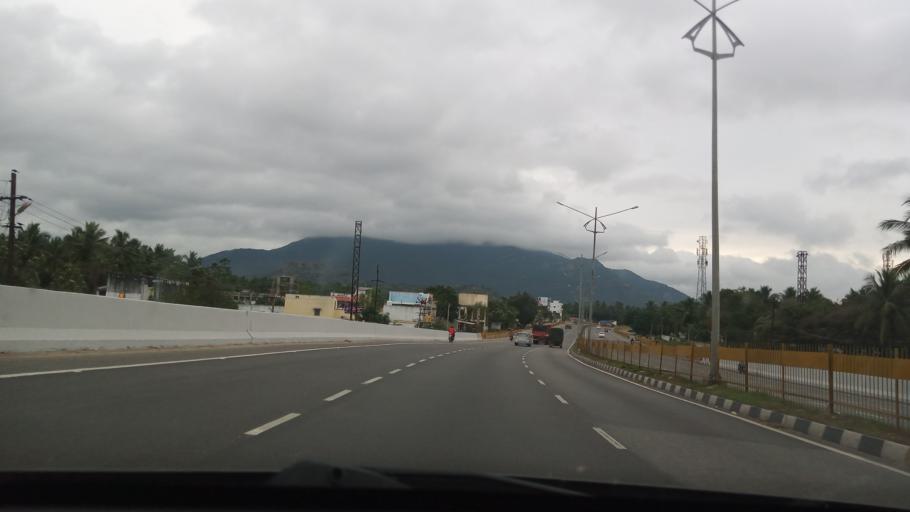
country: IN
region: Tamil Nadu
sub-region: Vellore
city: Ambur
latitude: 12.7449
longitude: 78.6961
